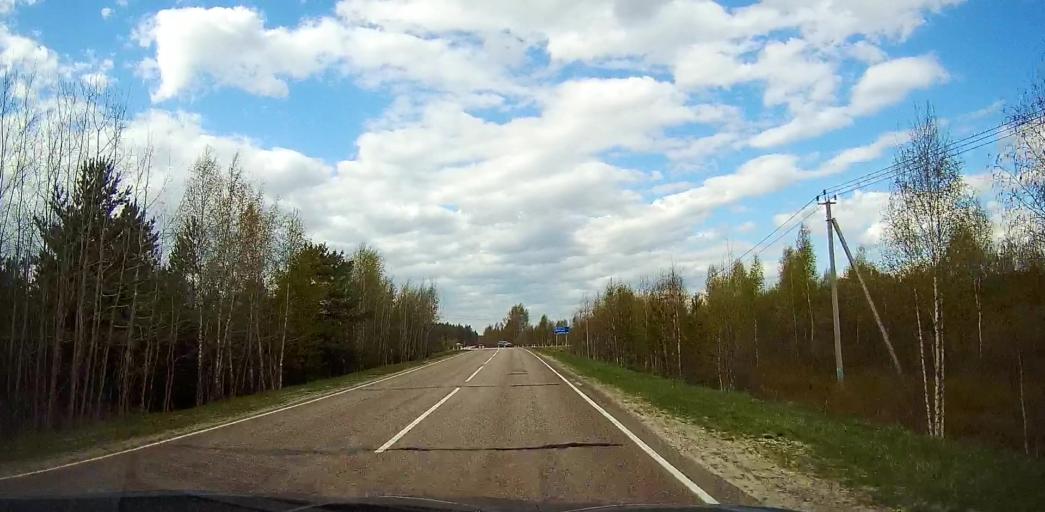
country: RU
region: Moskovskaya
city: Rakhmanovo
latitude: 55.6764
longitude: 38.6450
